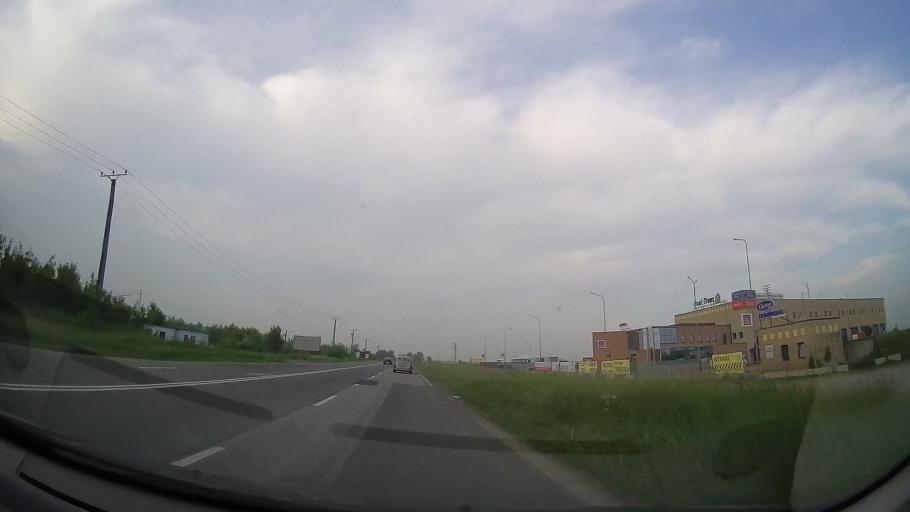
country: RO
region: Timis
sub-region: Comuna Giroc
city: Chisoda
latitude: 45.6960
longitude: 21.1783
